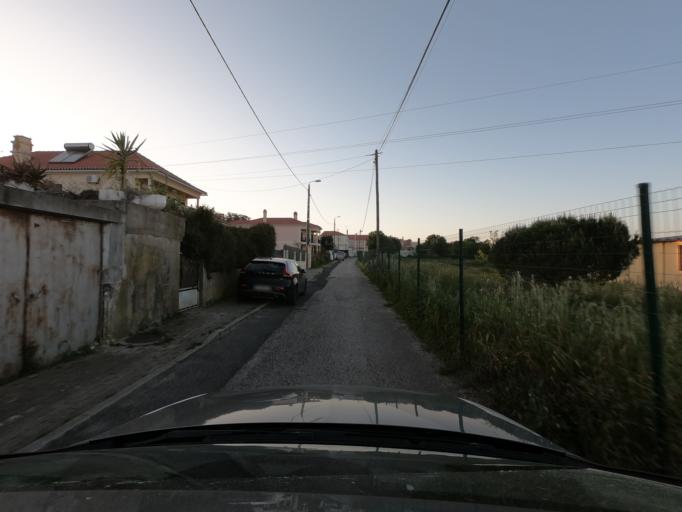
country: PT
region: Lisbon
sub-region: Sintra
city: Rio de Mouro
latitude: 38.7536
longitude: -9.3539
